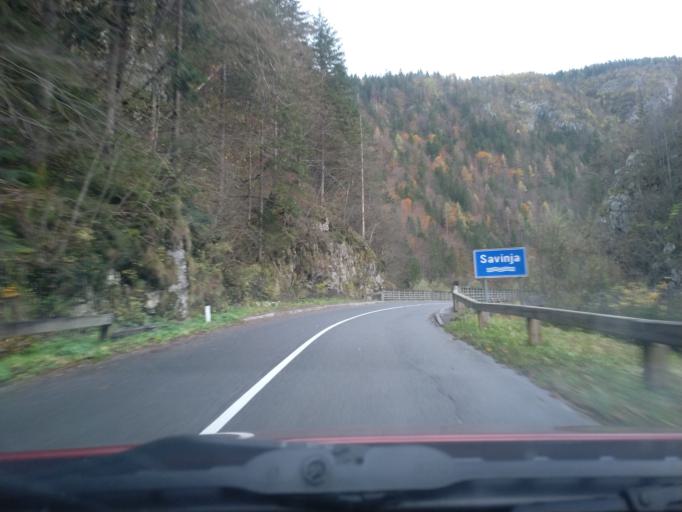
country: SI
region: Luce
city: Luce
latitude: 46.3657
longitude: 14.7322
